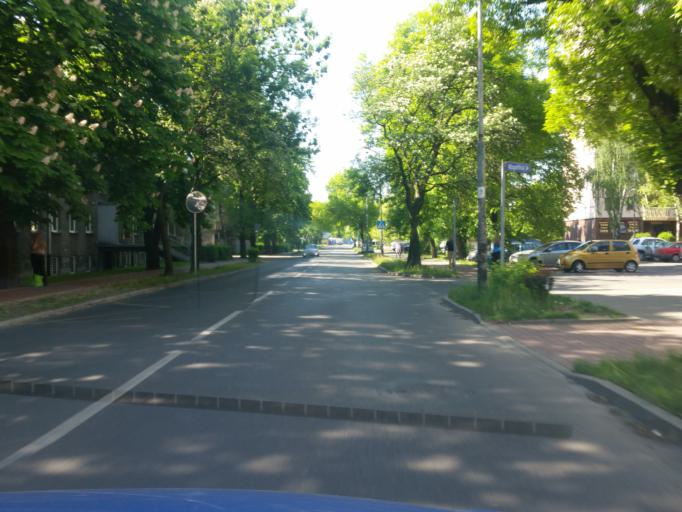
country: PL
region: Silesian Voivodeship
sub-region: Sosnowiec
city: Sosnowiec
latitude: 50.2716
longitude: 19.1283
